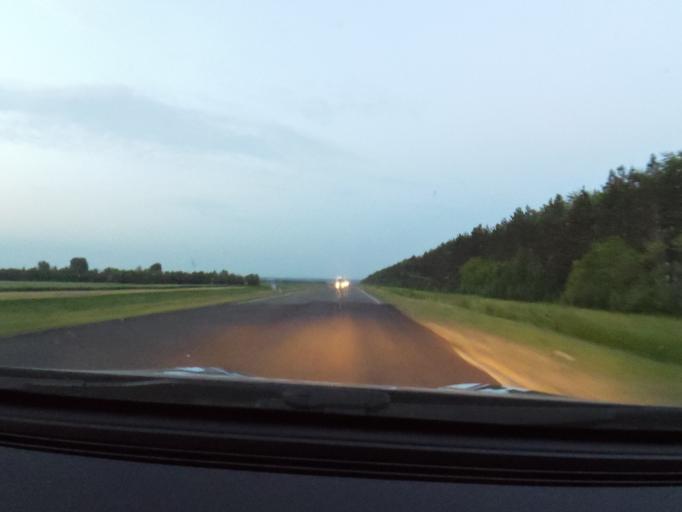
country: RU
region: Bashkortostan
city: Duvan
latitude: 56.0766
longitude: 58.1203
